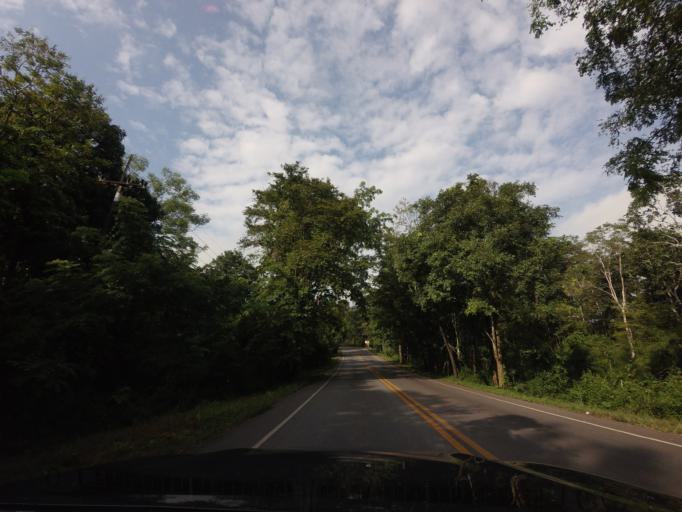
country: TH
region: Nong Khai
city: Pho Tak
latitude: 17.8064
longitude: 102.3260
